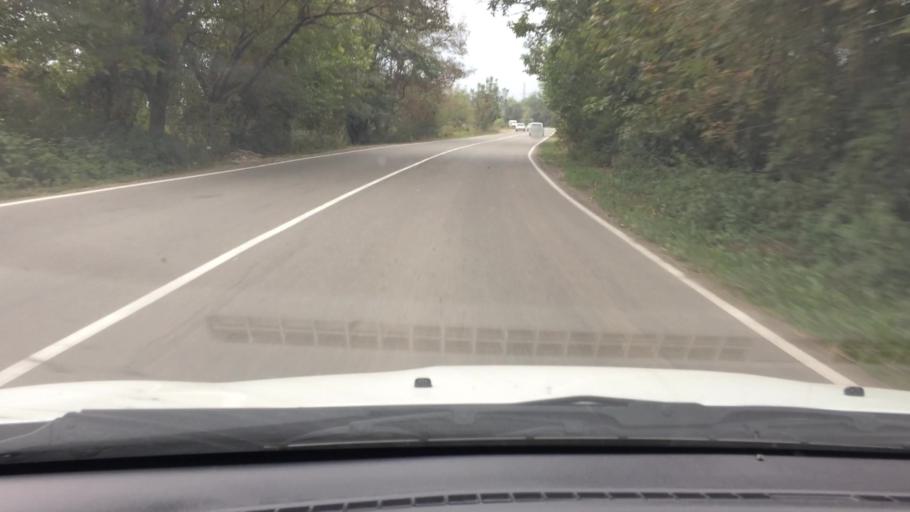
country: AM
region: Tavush
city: Bagratashen
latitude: 41.2611
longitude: 44.7960
